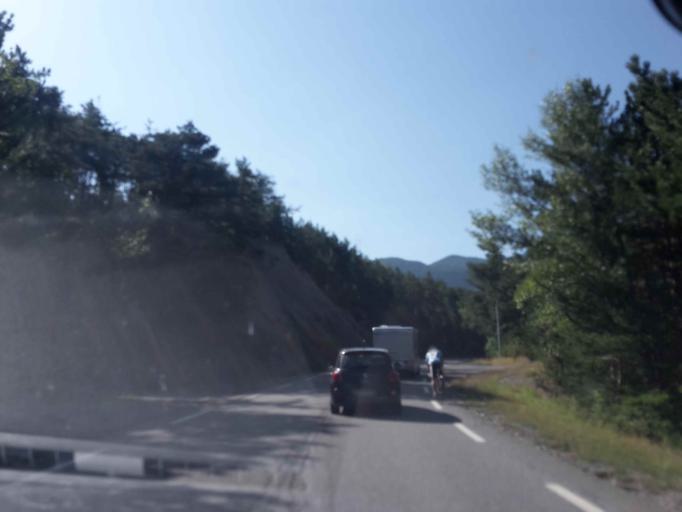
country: FR
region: Provence-Alpes-Cote d'Azur
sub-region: Departement des Hautes-Alpes
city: Guillestre
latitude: 44.6477
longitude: 6.6555
